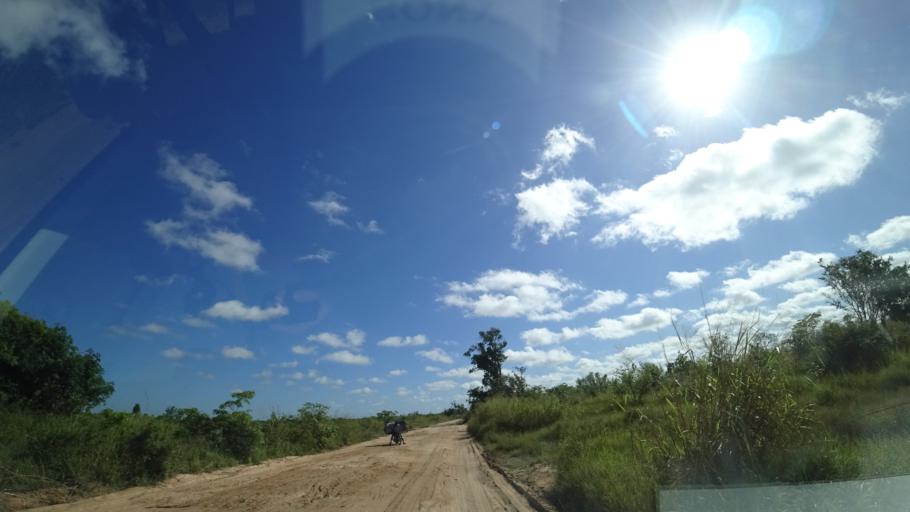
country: MZ
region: Sofala
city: Dondo
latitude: -19.4140
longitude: 34.7099
